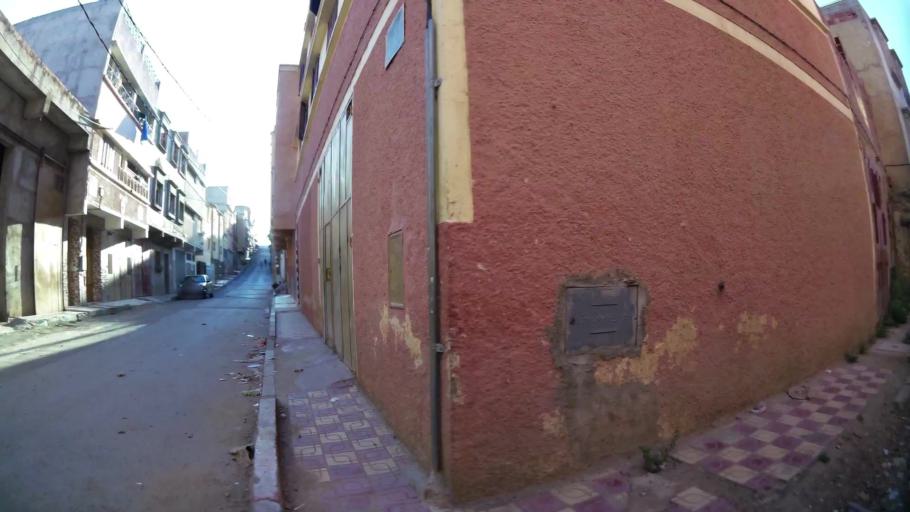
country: MA
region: Oriental
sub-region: Berkane-Taourirt
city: Berkane
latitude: 34.9262
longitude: -2.3193
